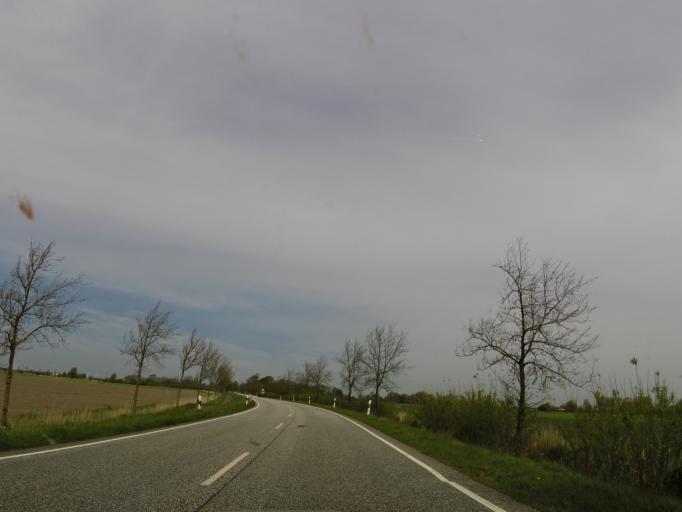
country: DE
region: Schleswig-Holstein
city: Tonning
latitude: 54.3467
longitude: 8.9708
